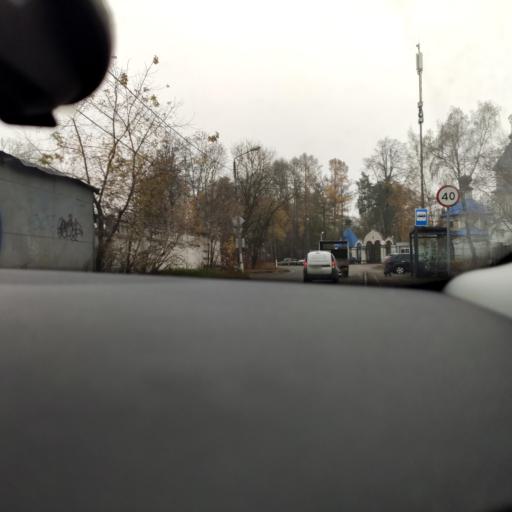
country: RU
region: Moskovskaya
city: Nakhabino
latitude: 55.8422
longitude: 37.1577
